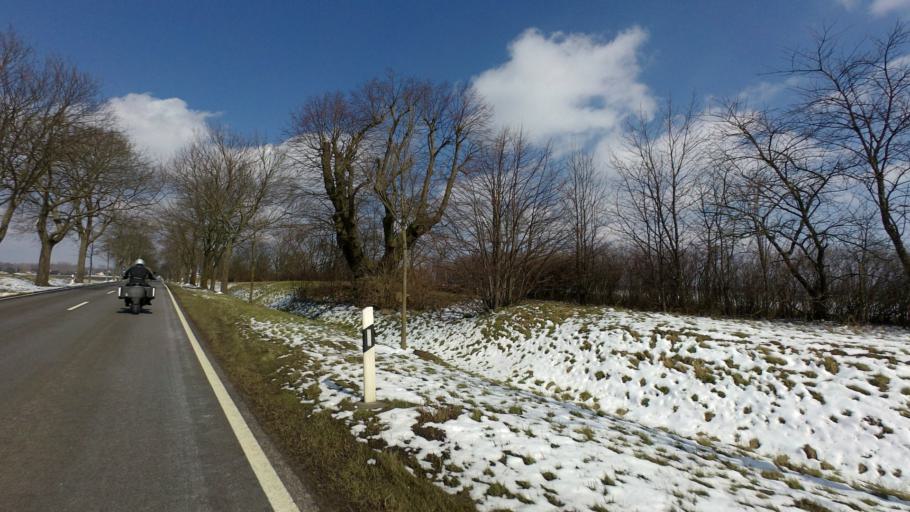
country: DE
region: Brandenburg
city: Eberswalde
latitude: 52.7626
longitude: 13.8404
